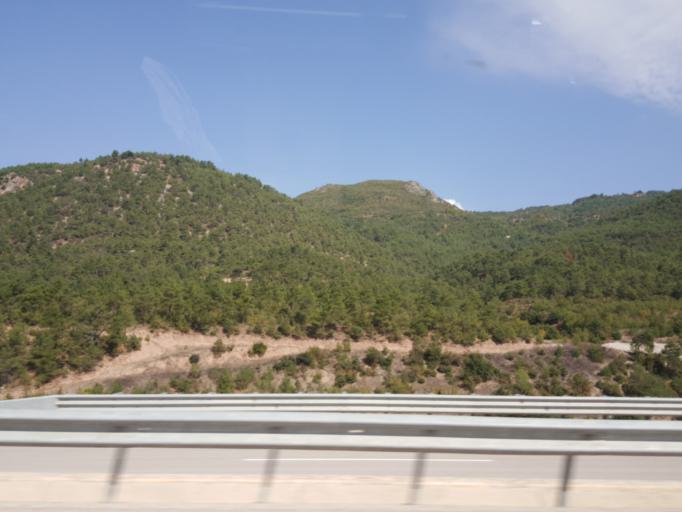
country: TR
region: Tokat
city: Basciftlik
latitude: 40.4576
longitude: 37.0475
